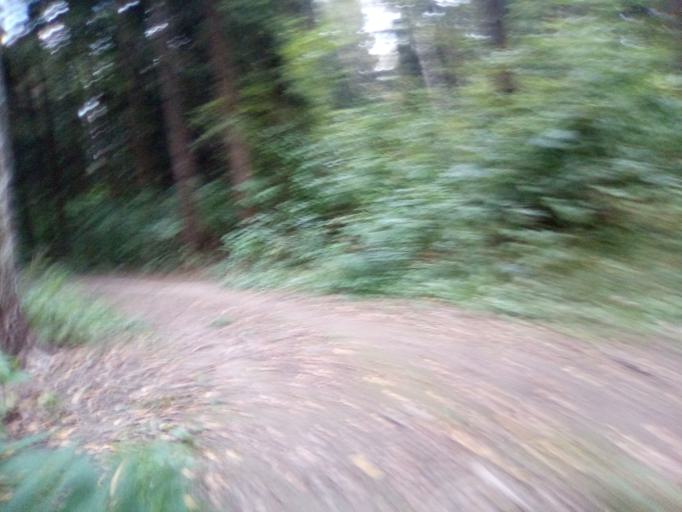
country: RU
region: Moscow
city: Novo-Peredelkino
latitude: 55.6211
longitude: 37.3273
